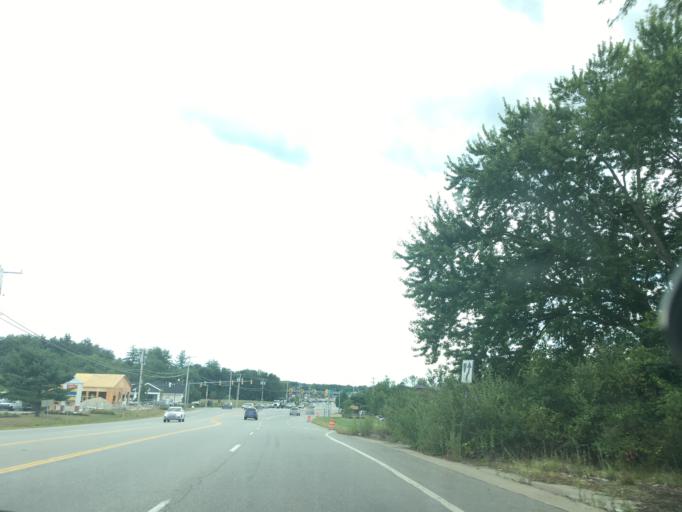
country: US
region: New Hampshire
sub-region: Rockingham County
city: Exeter
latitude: 42.9981
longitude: -70.9236
